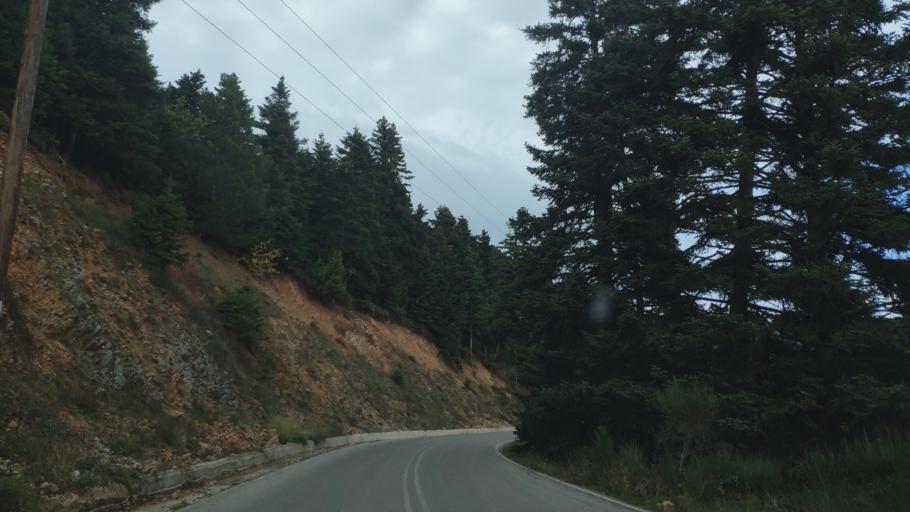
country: GR
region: Central Greece
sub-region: Nomos Fokidos
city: Amfissa
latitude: 38.6944
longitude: 22.3190
